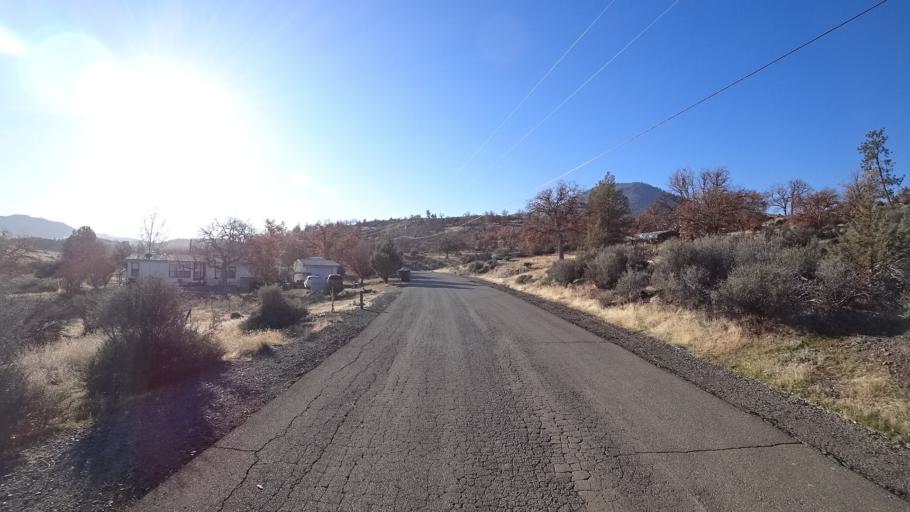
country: US
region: California
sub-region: Siskiyou County
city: Montague
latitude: 41.8941
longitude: -122.4967
